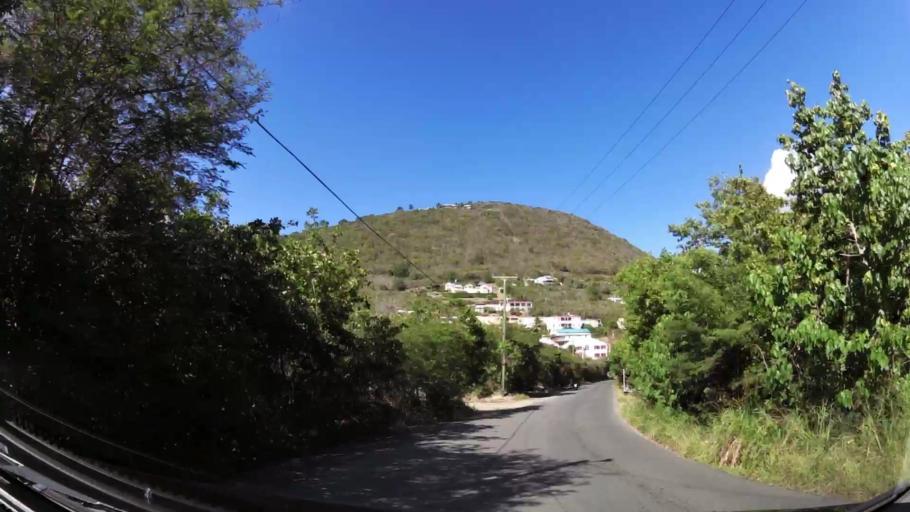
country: VG
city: Road Town
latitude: 18.3862
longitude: -64.6985
